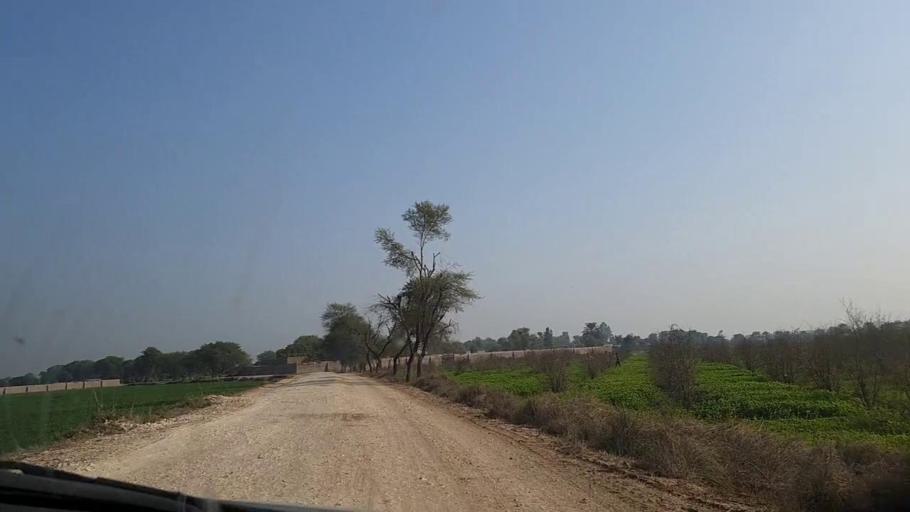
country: PK
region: Sindh
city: Moro
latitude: 26.8144
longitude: 67.9582
